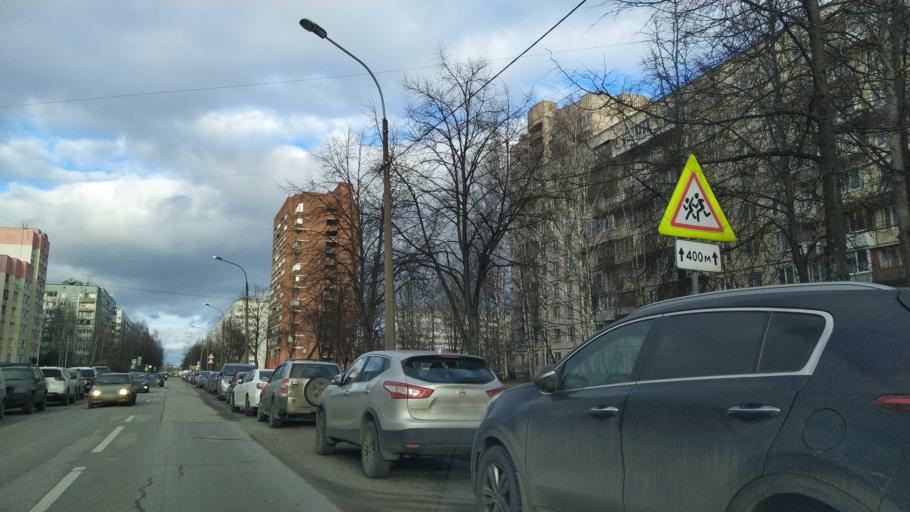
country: RU
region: Leningrad
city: Parnas
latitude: 60.0486
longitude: 30.3682
